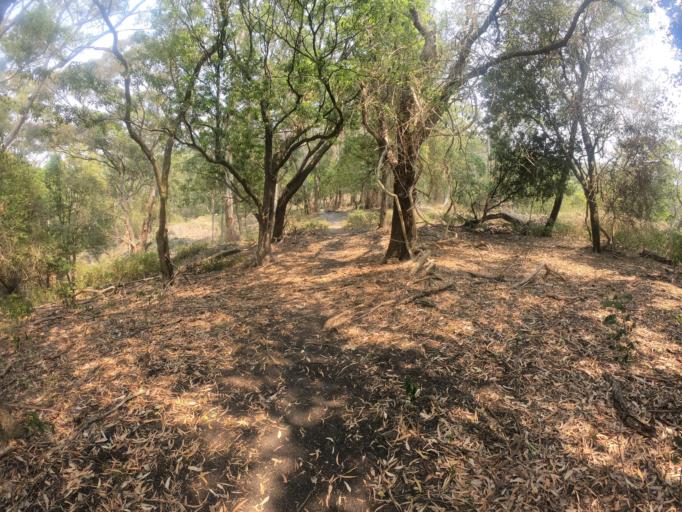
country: AU
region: New South Wales
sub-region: Wollongong
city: Keiraville
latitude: -34.4081
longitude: 150.8630
